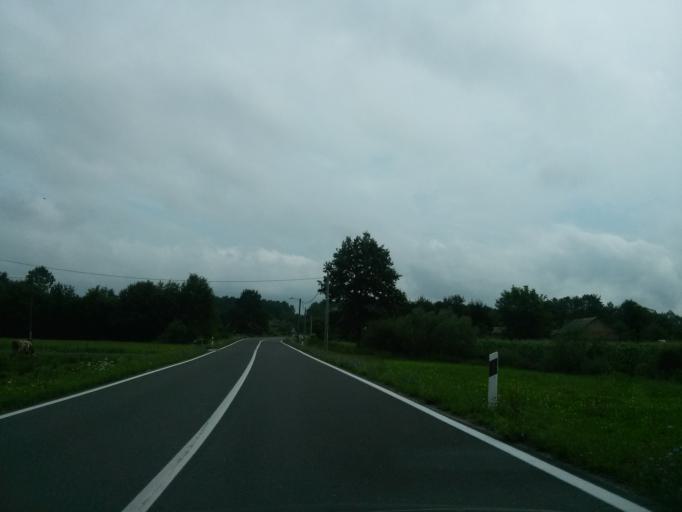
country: HR
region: Sisacko-Moslavacka
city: Glina
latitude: 45.3386
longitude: 16.0332
